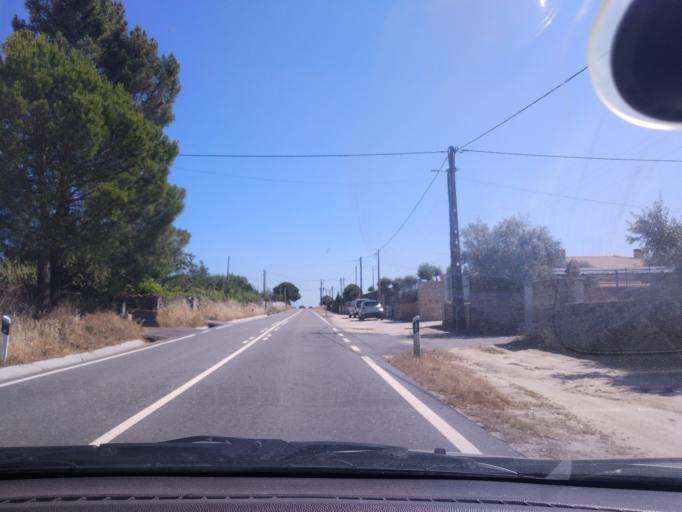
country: PT
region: Guarda
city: Alcains
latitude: 39.9265
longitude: -7.4649
